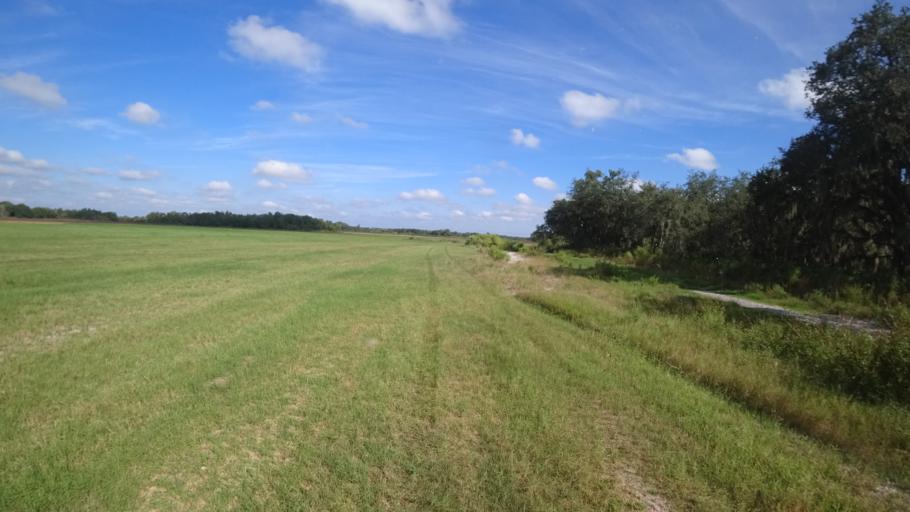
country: US
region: Florida
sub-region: Sarasota County
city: Lake Sarasota
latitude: 27.3725
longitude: -82.1633
